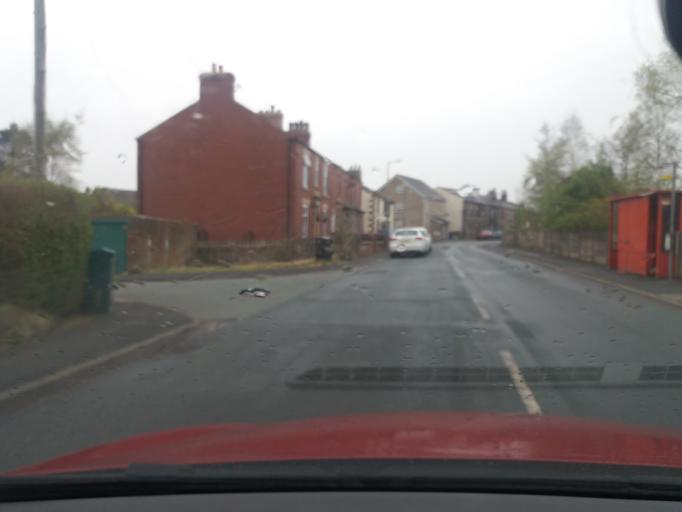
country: GB
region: England
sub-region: Lancashire
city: Clayton-le-Woods
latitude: 53.6879
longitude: -2.6358
